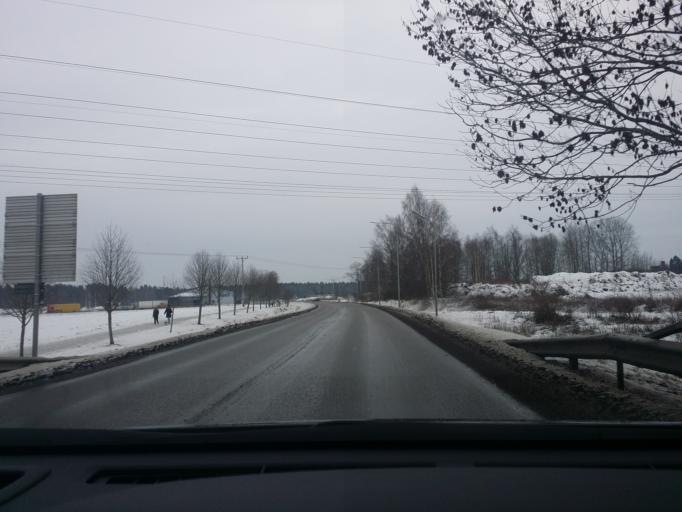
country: SE
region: Vaestra Goetaland
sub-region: Mariestads Kommun
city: Mariestad
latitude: 58.6923
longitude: 13.8262
